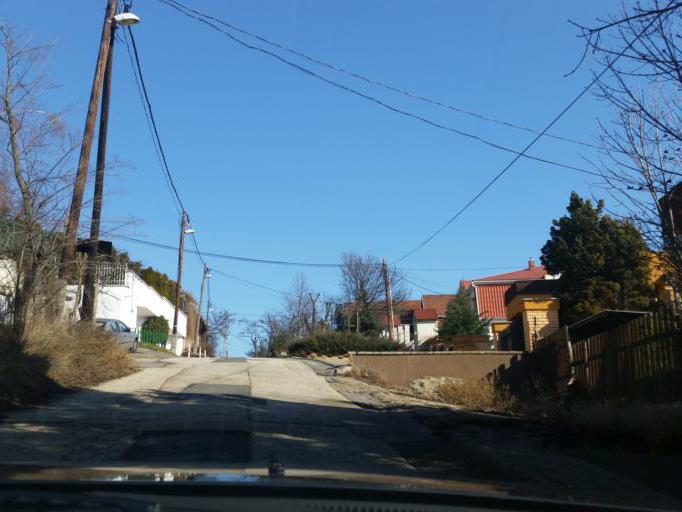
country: HU
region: Budapest
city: Budapest II. keruelet
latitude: 47.5341
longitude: 19.0011
